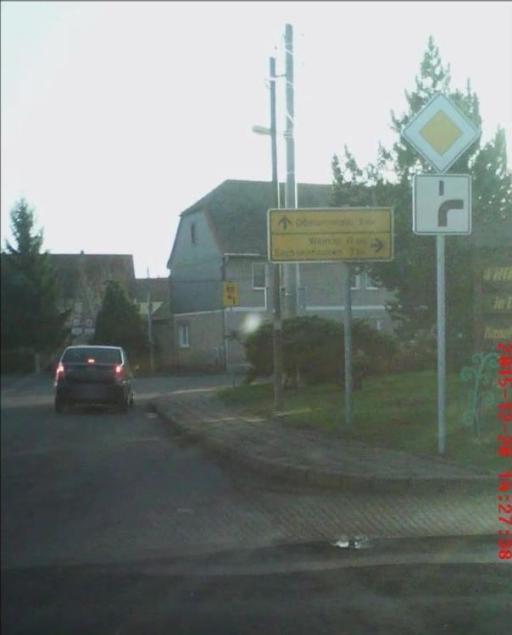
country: DE
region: Thuringia
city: Liebstedt
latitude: 51.0488
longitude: 11.4109
